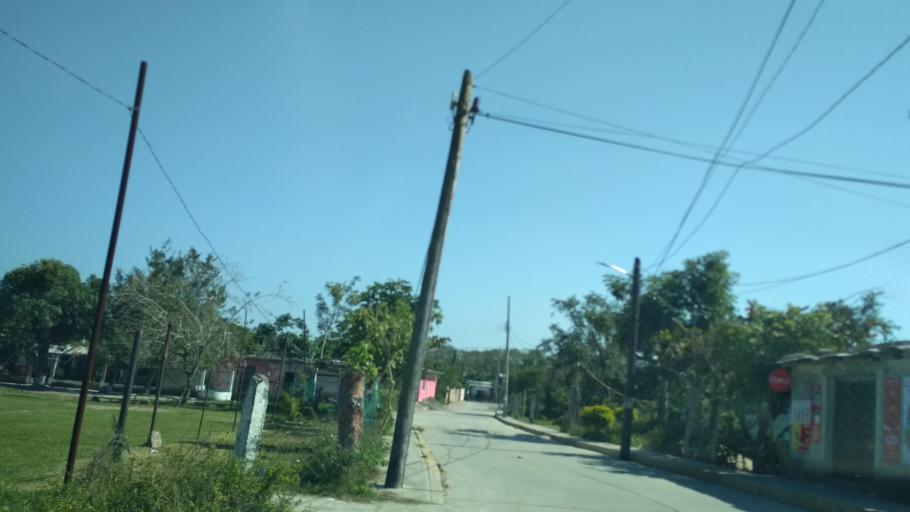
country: MX
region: Veracruz
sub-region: Papantla
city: El Chote
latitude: 20.4002
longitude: -97.3347
